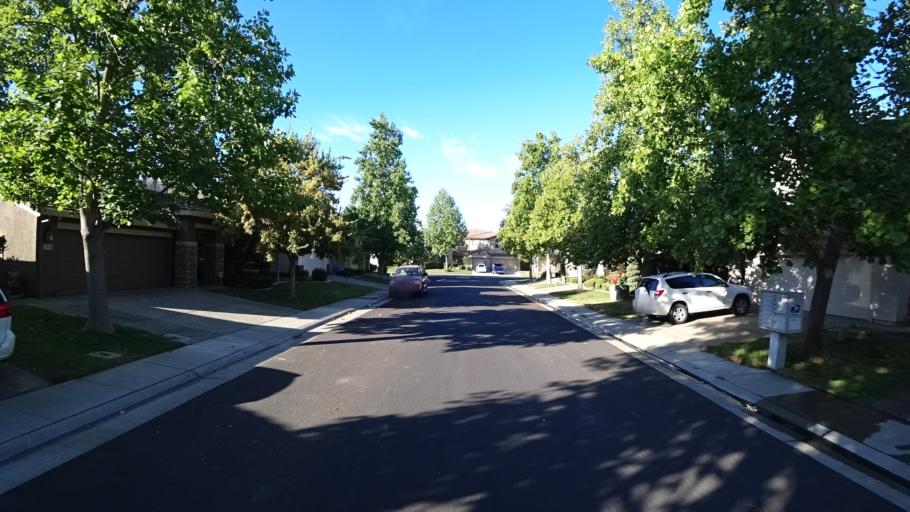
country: US
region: California
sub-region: Sacramento County
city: Laguna
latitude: 38.4043
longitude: -121.4780
